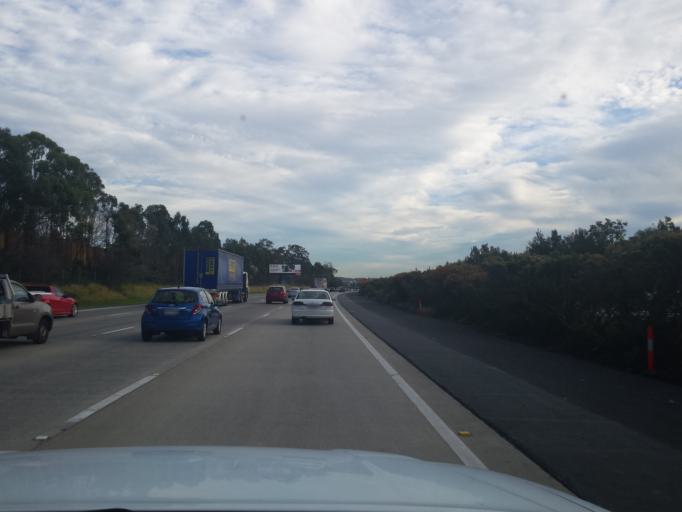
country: AU
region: Queensland
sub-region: Gold Coast
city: Ormeau Hills
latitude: -27.7779
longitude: 153.2522
